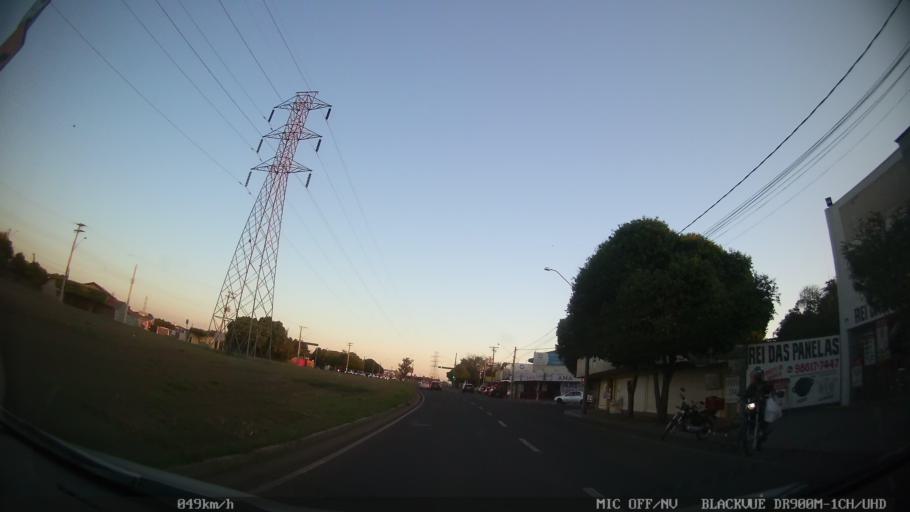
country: BR
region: Sao Paulo
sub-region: Sao Jose Do Rio Preto
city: Sao Jose do Rio Preto
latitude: -20.7927
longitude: -49.3447
